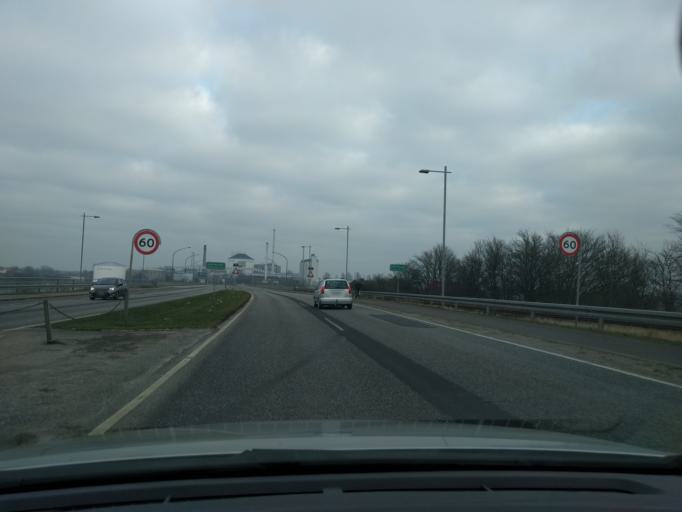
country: DK
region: Zealand
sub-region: Guldborgsund Kommune
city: Nykobing Falster
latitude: 54.7578
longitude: 11.8622
